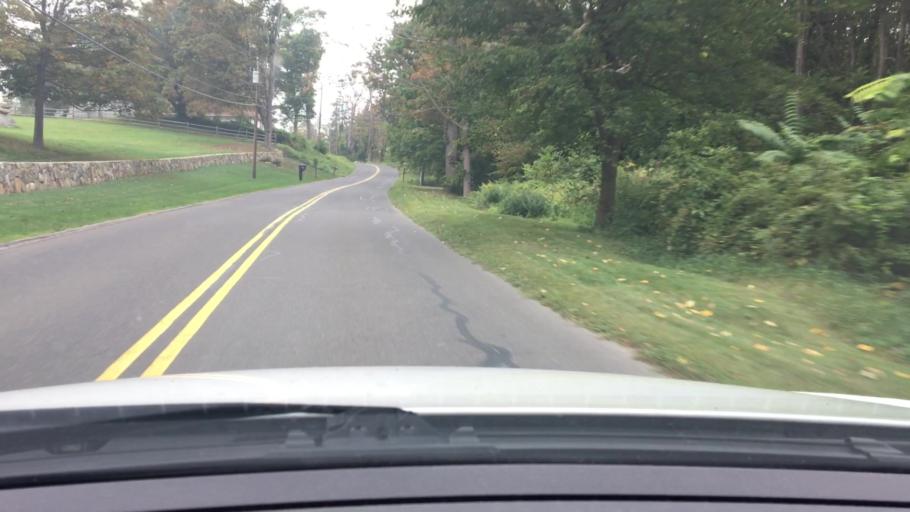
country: US
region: Connecticut
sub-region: Fairfield County
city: Newtown
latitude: 41.4557
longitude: -73.3560
